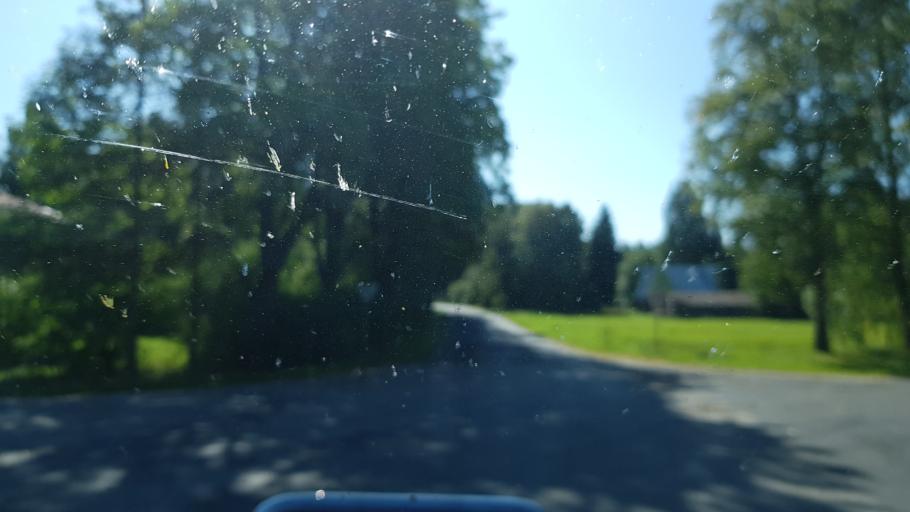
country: EE
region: Polvamaa
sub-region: Raepina vald
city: Rapina
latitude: 58.2105
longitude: 27.2561
